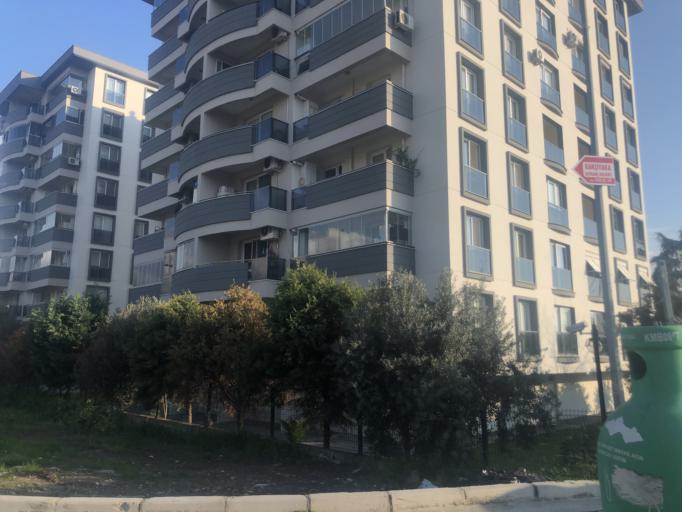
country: TR
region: Izmir
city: Karsiyaka
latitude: 38.4886
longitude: 27.0537
